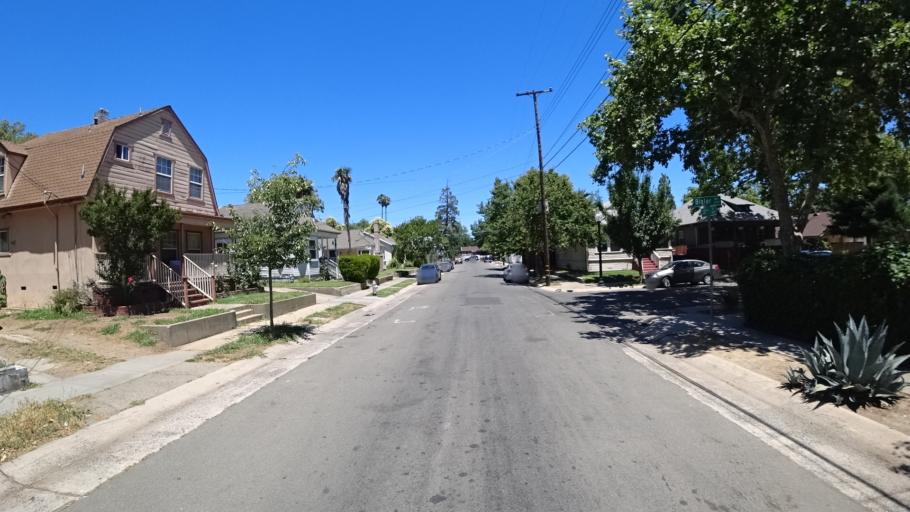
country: US
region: California
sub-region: Sacramento County
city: Sacramento
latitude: 38.5471
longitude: -121.4671
